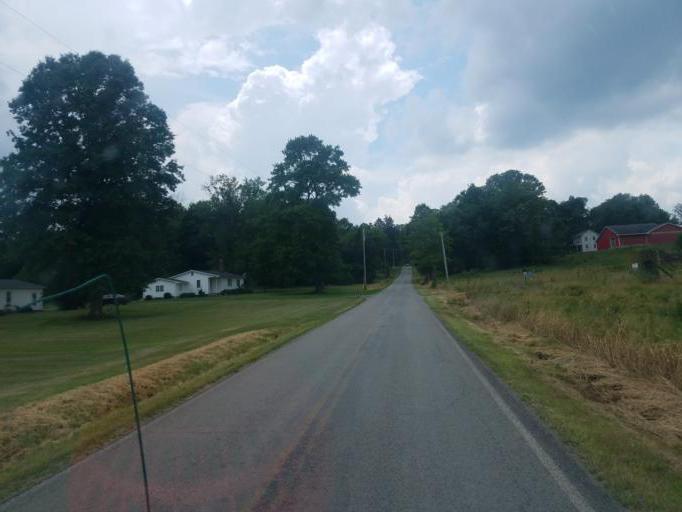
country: US
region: Ohio
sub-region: Mahoning County
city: Canfield
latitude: 40.9583
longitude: -80.7809
